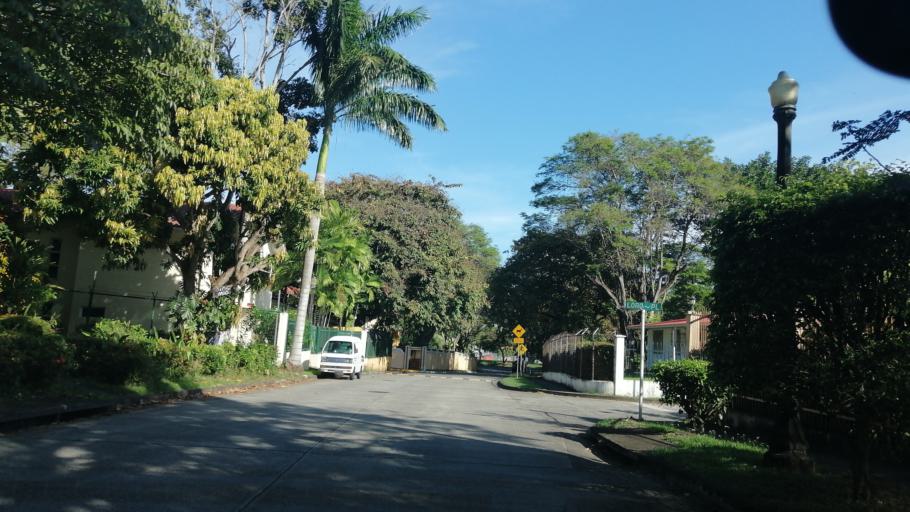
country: PA
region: Panama
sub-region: Distrito de Panama
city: Ancon
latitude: 8.9643
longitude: -79.5473
